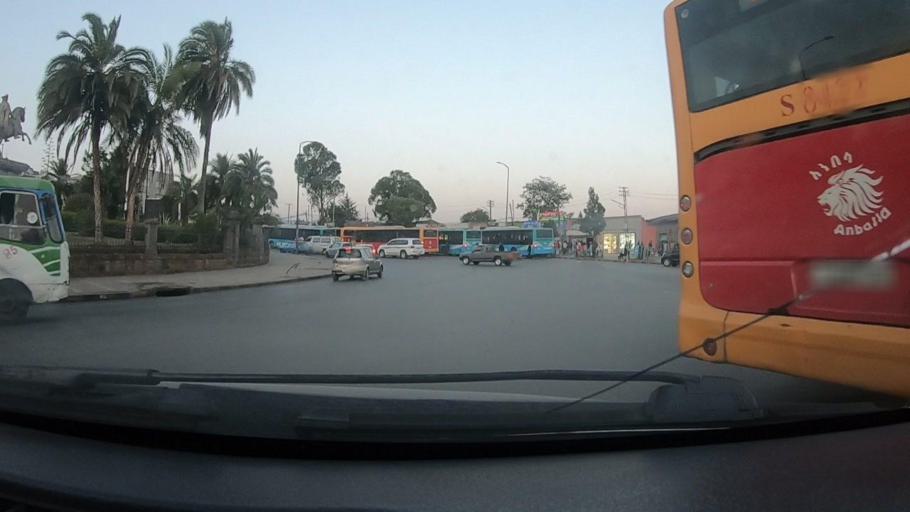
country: ET
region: Adis Abeba
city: Addis Ababa
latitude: 9.0350
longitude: 38.7519
